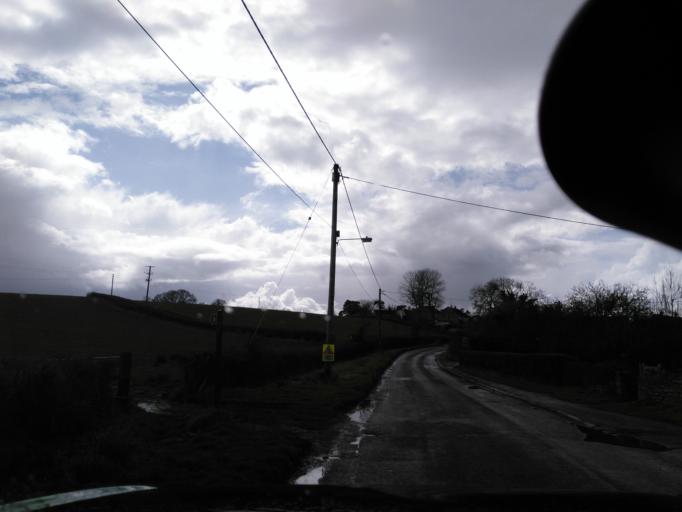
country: GB
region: England
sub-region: Wiltshire
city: Atworth
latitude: 51.3945
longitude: -2.1829
